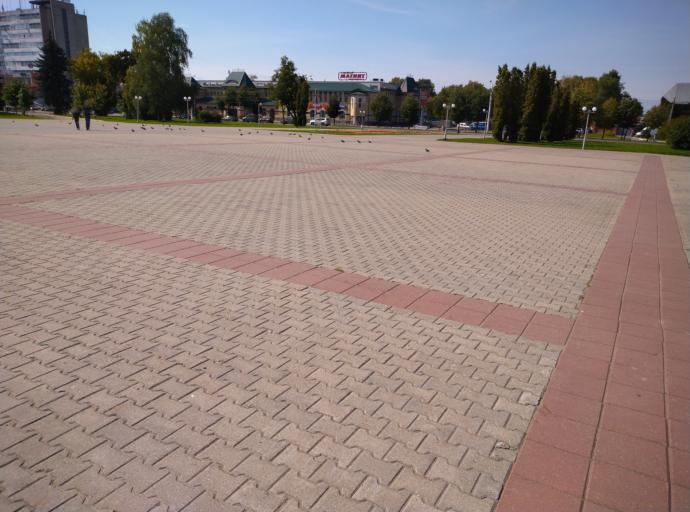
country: RU
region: Kostroma
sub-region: Kostromskoy Rayon
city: Kostroma
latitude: 57.7727
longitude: 40.9400
